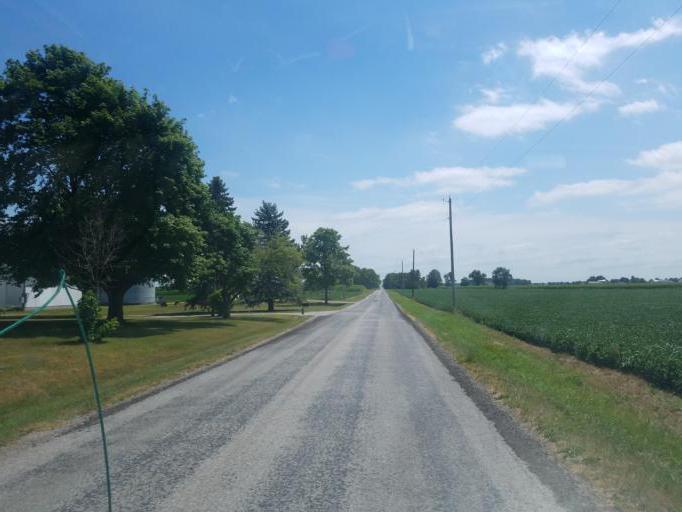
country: US
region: Indiana
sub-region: Allen County
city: Harlan
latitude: 41.1950
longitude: -84.8842
